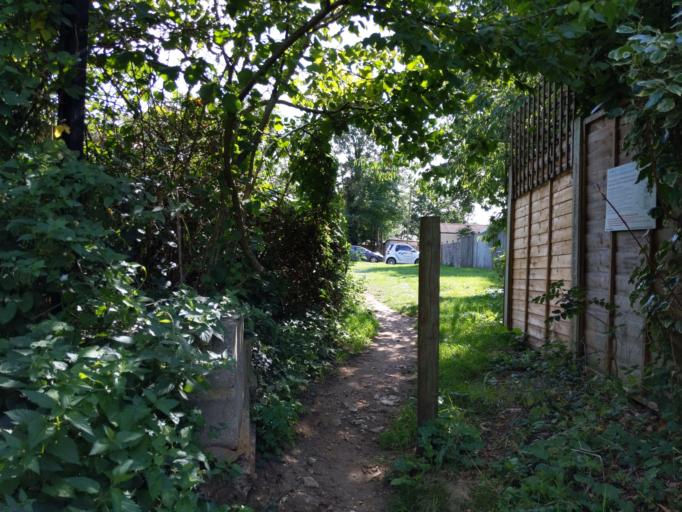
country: GB
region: England
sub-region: Oxfordshire
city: Radley
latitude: 51.7041
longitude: -1.2430
